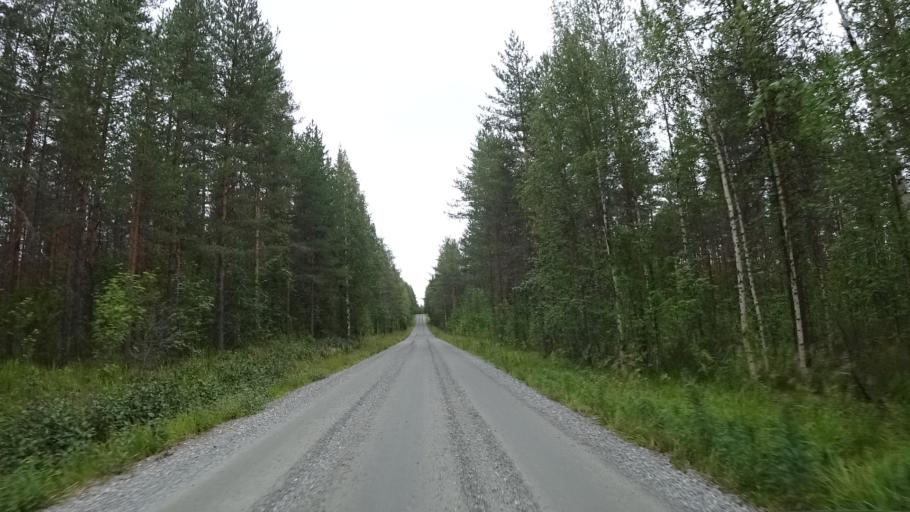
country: FI
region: North Karelia
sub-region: Pielisen Karjala
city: Lieksa
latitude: 63.3763
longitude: 30.3574
